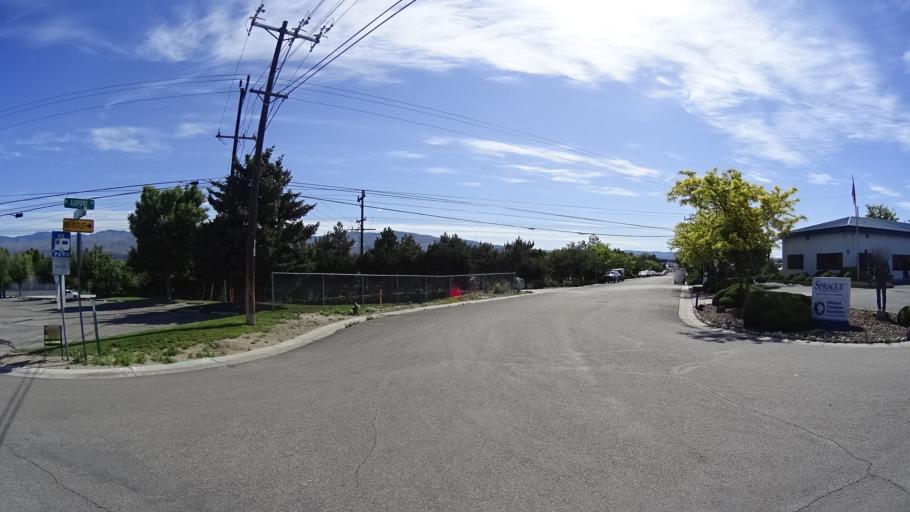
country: US
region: Idaho
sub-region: Ada County
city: Boise
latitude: 43.5681
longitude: -116.2075
